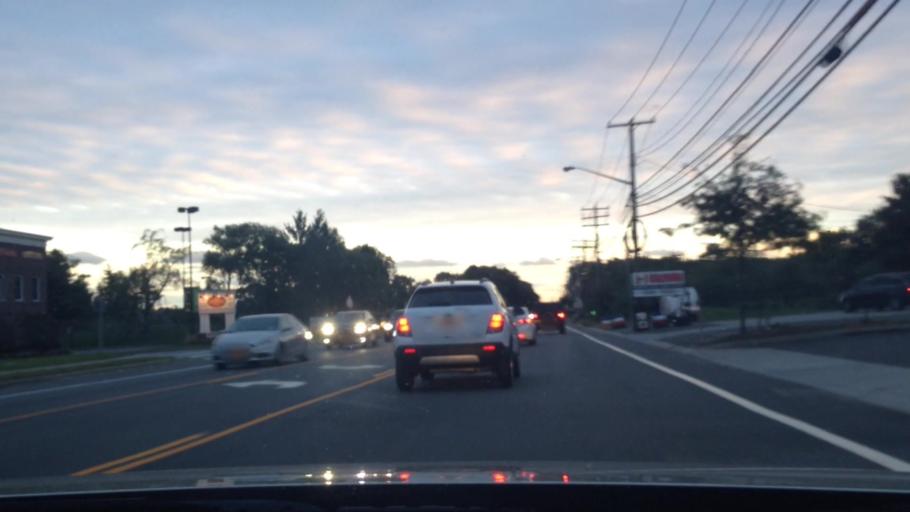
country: US
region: New York
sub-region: Suffolk County
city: Coram
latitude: 40.8455
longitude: -72.9971
